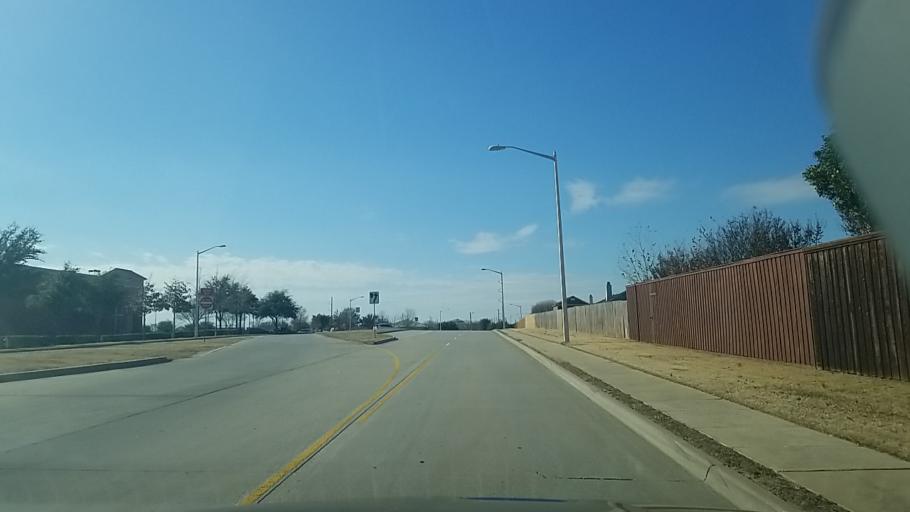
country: US
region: Texas
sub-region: Denton County
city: Corinth
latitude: 33.1467
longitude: -97.1011
